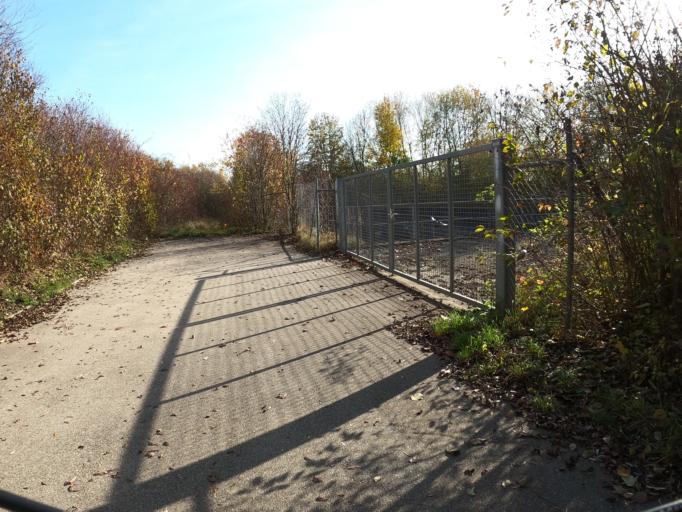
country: DE
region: Bavaria
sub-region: Swabia
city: Nersingen
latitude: 48.4513
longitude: 10.1051
